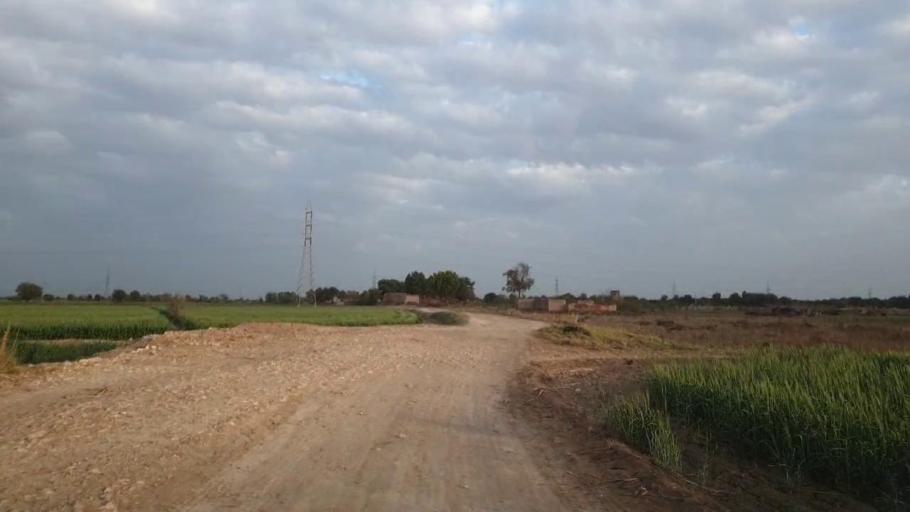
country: PK
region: Sindh
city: Matiari
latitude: 25.5670
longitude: 68.4446
